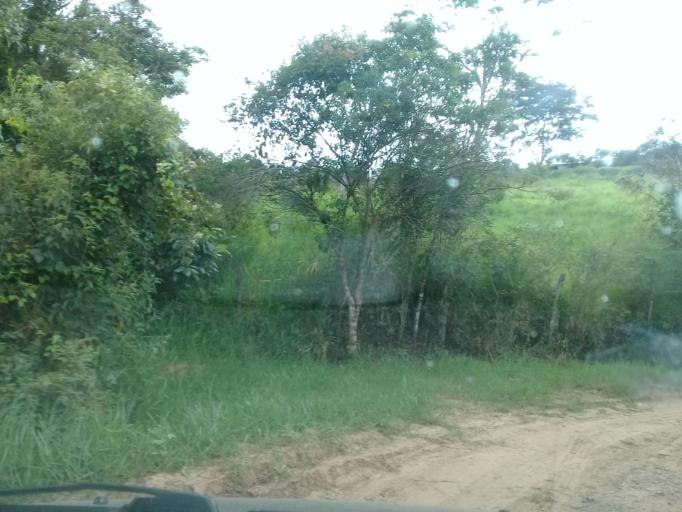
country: CO
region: Cundinamarca
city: Guaduas
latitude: 5.1202
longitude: -74.6060
